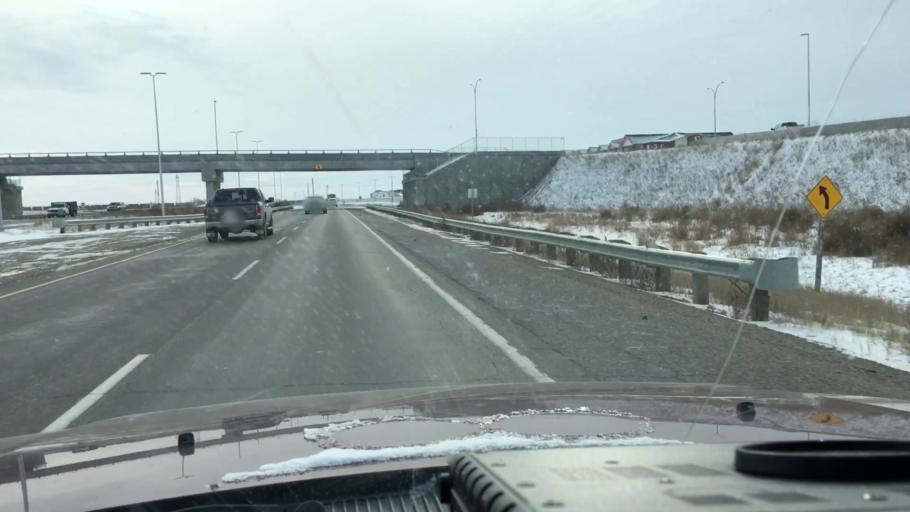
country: CA
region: Saskatchewan
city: Saskatoon
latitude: 52.0793
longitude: -106.6050
